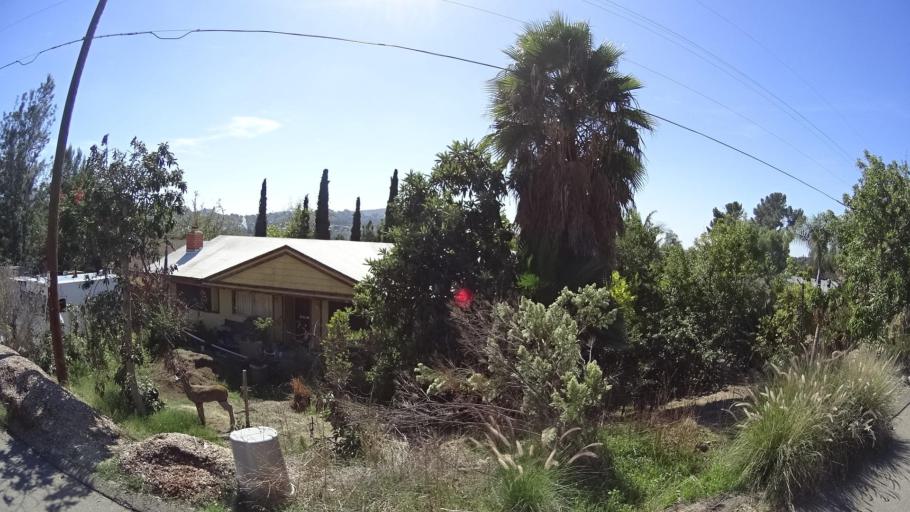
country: US
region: California
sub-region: San Diego County
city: Casa de Oro-Mount Helix
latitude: 32.7551
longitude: -116.9807
